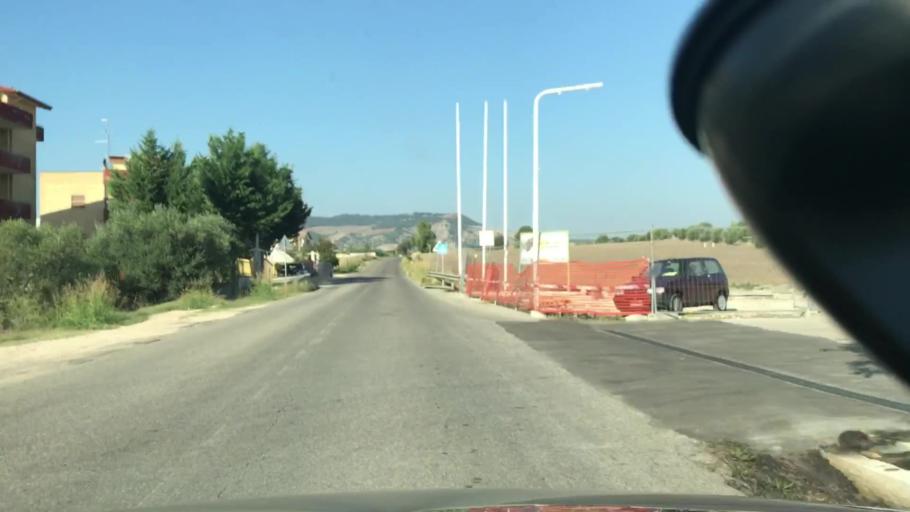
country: IT
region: Basilicate
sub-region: Provincia di Matera
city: La Martella
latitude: 40.6588
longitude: 16.5390
